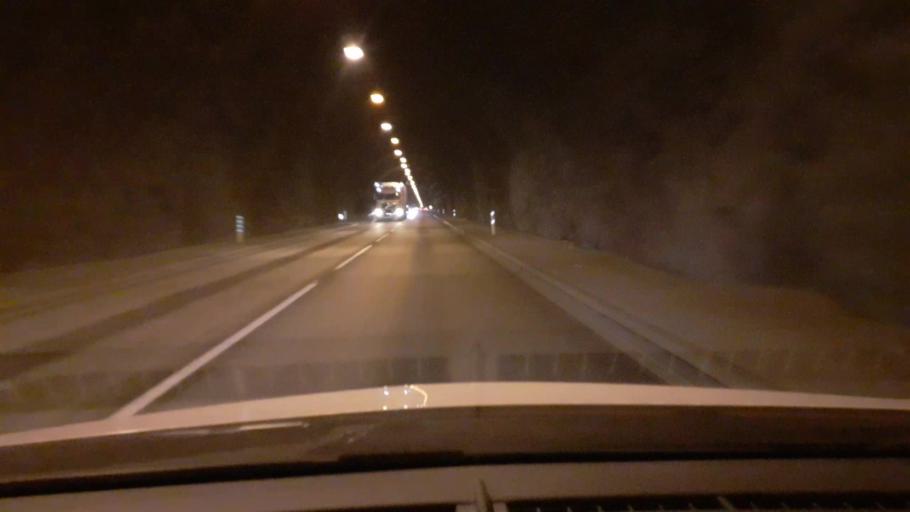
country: IS
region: Capital Region
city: Reykjavik
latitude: 64.2931
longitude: -21.8650
